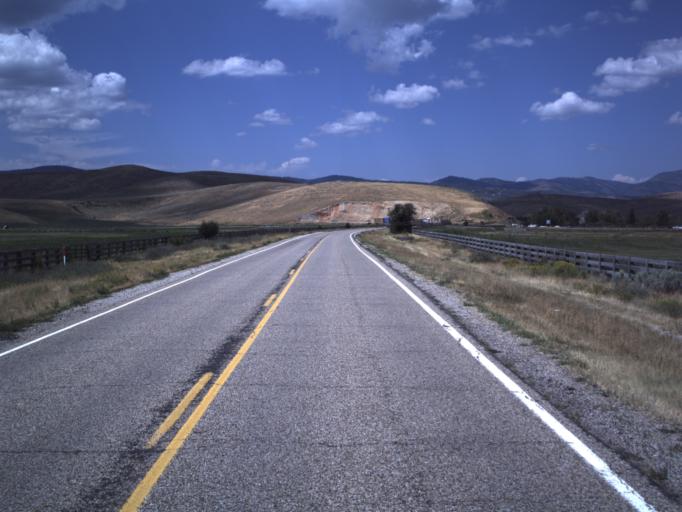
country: US
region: Utah
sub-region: Rich County
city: Randolph
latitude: 41.8420
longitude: -111.3459
